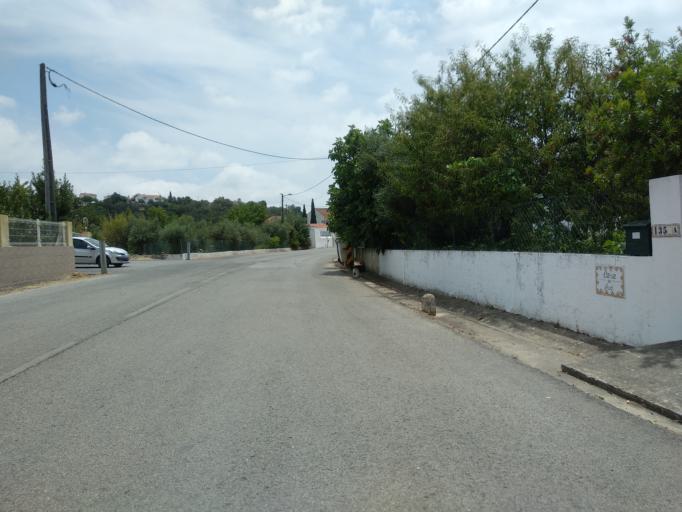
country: PT
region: Faro
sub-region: Sao Bras de Alportel
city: Sao Bras de Alportel
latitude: 37.1682
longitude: -7.8907
